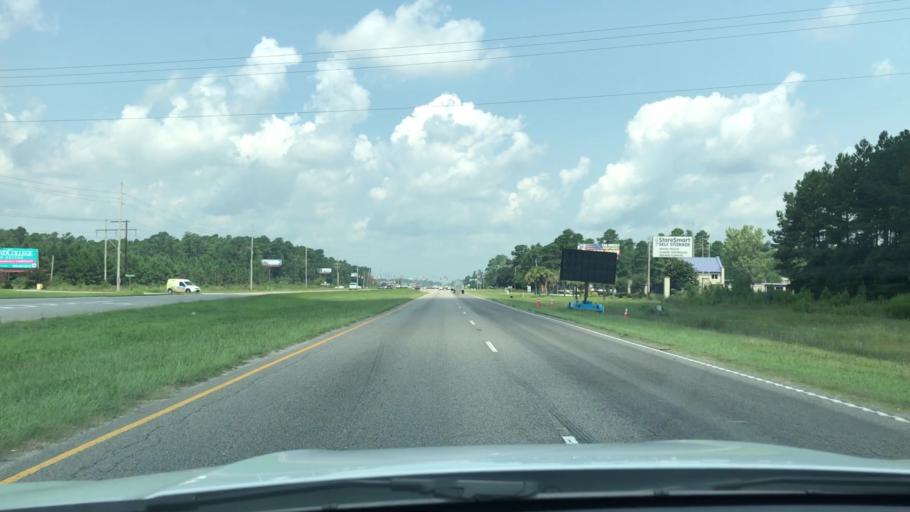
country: US
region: South Carolina
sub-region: Horry County
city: Red Hill
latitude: 33.7792
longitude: -78.9864
